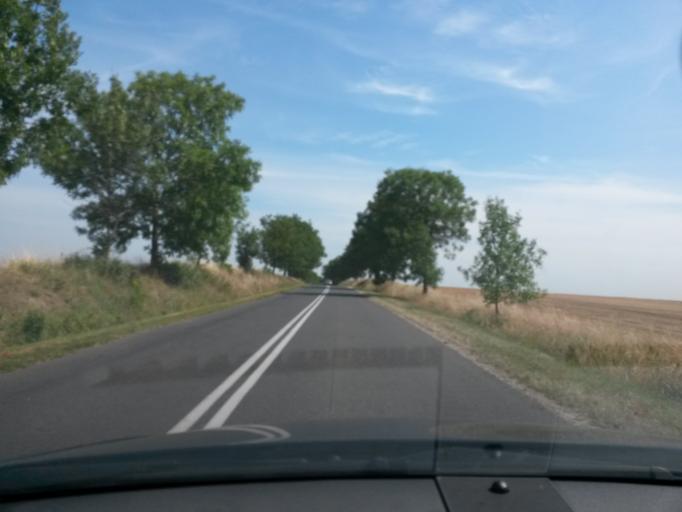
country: PL
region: Lower Silesian Voivodeship
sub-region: Powiat jaworski
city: Jawor
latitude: 51.0657
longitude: 16.2221
